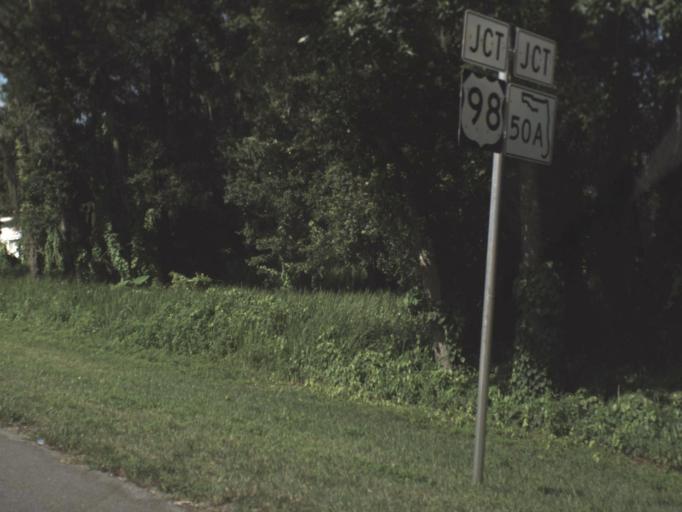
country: US
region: Florida
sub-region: Hernando County
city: Brooksville
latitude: 28.5577
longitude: -82.3977
